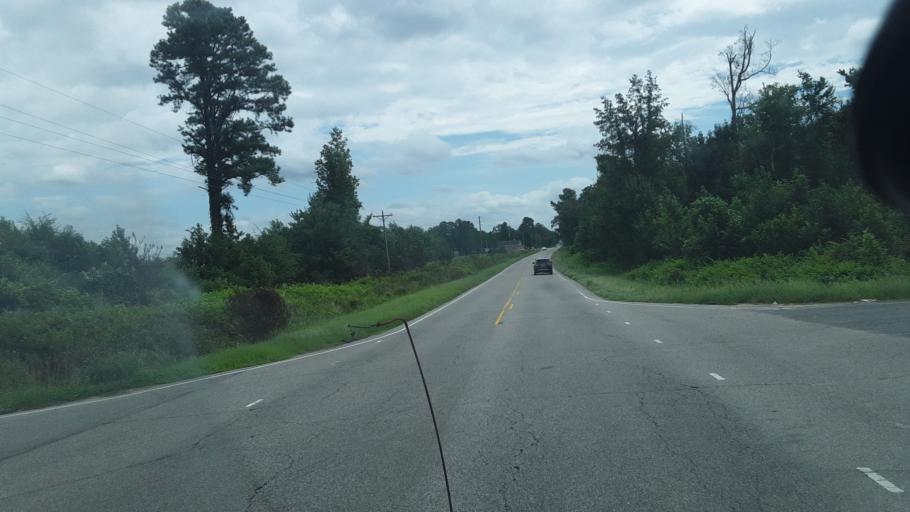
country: US
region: North Carolina
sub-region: Robeson County
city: Maxton
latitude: 34.6590
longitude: -79.3846
